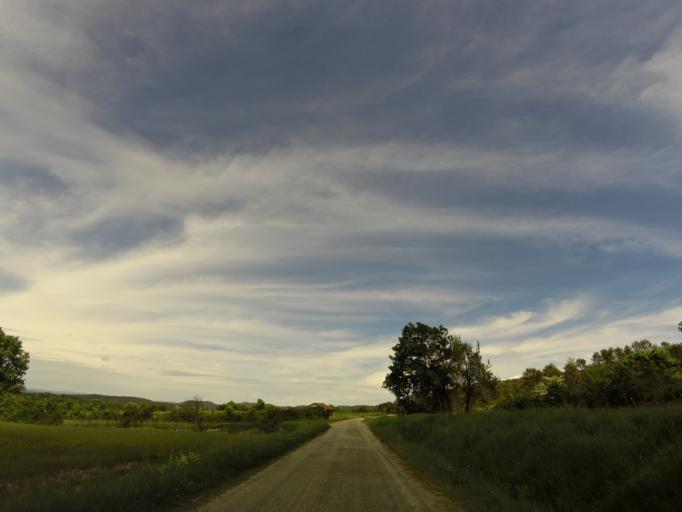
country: FR
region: Languedoc-Roussillon
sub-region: Departement du Gard
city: Quissac
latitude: 43.8667
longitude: 4.0268
